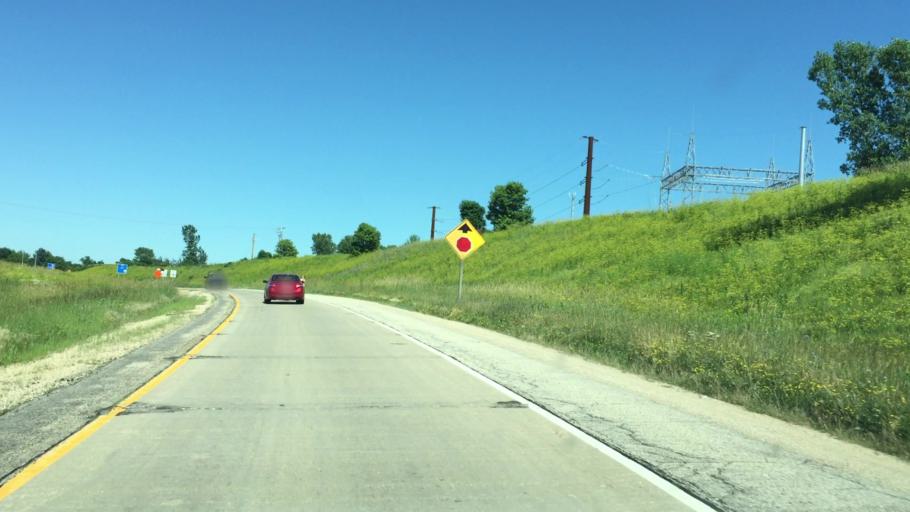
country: US
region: Wisconsin
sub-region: Dane County
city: Verona
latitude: 42.9732
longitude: -89.5168
